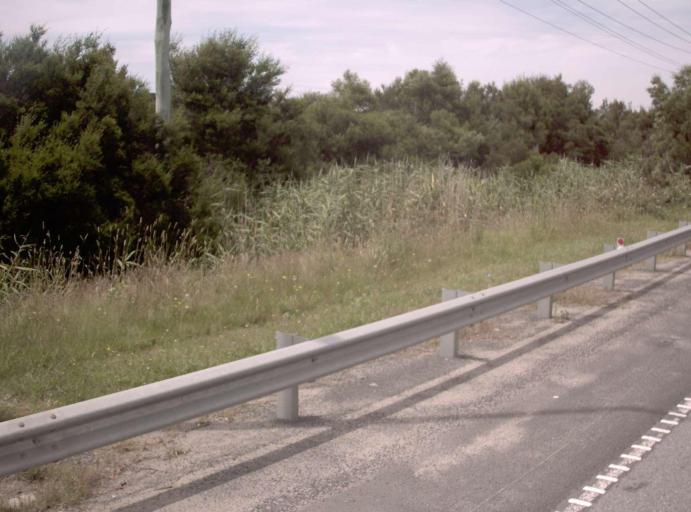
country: AU
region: Victoria
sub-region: Mornington Peninsula
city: Tyabb
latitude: -38.2731
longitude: 145.1898
